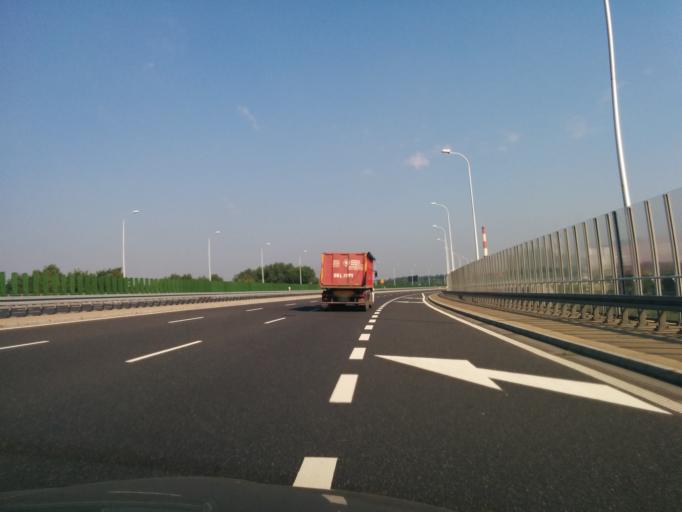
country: PL
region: Silesian Voivodeship
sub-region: Gliwice
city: Gliwice
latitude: 50.2843
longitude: 18.7178
